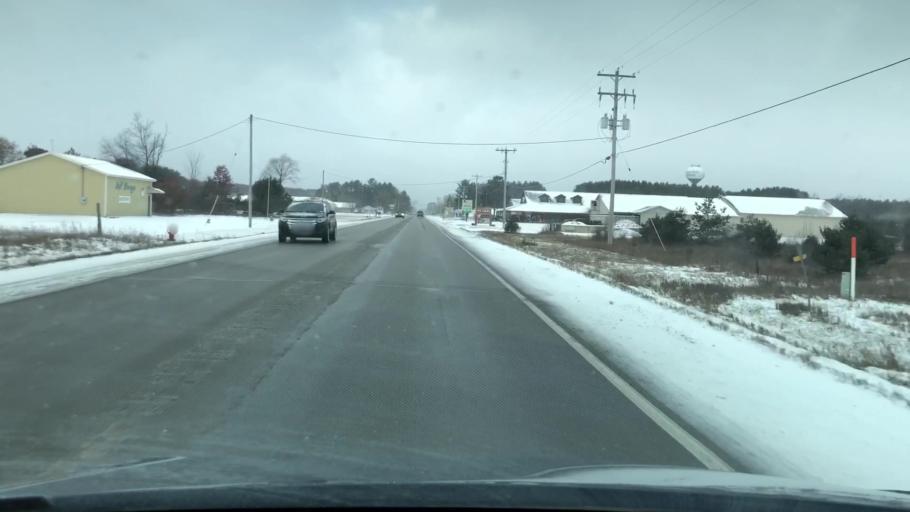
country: US
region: Michigan
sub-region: Wexford County
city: Cadillac
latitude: 44.2813
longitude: -85.4305
